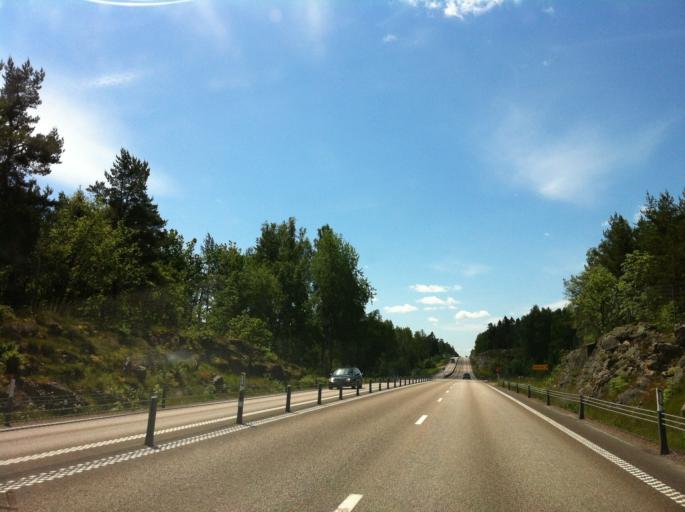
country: SE
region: Vaestra Goetaland
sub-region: Melleruds Kommun
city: Mellerud
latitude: 58.7560
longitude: 12.4894
